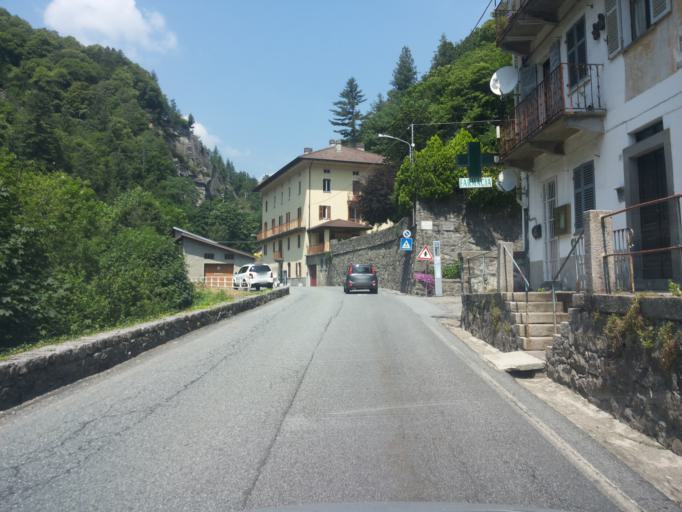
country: IT
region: Piedmont
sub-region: Provincia di Biella
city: San Paolo Cervo
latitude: 45.6476
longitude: 8.0173
